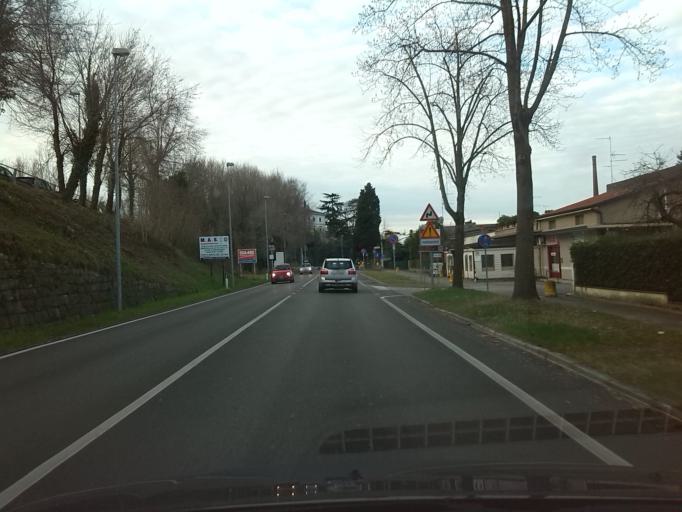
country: IT
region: Friuli Venezia Giulia
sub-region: Provincia di Gorizia
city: Sagrado
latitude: 45.8721
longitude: 13.4828
